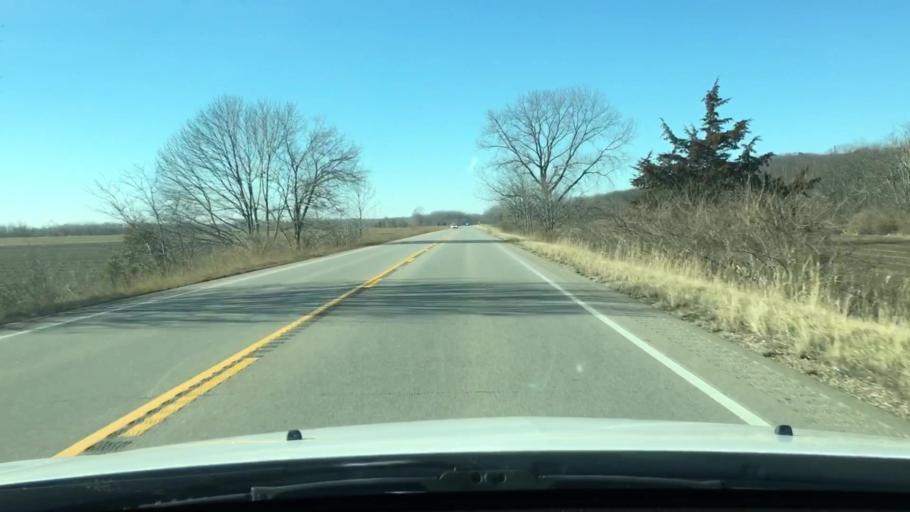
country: US
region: Illinois
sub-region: Peoria County
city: Glasford
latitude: 40.5524
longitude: -89.7970
